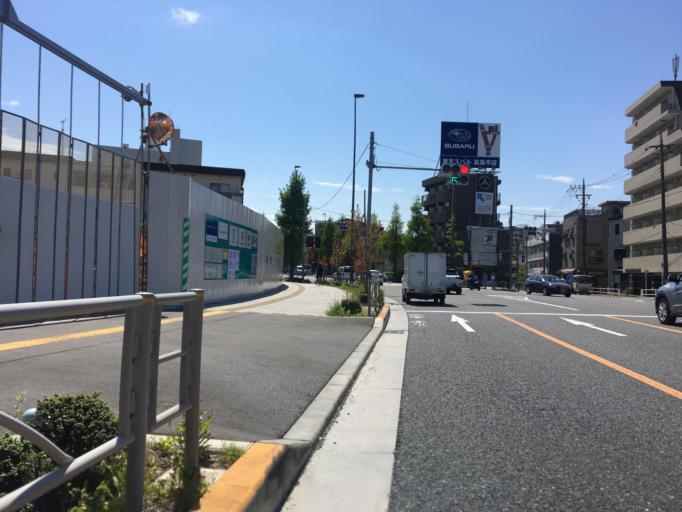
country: JP
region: Saitama
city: Shimotoda
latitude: 35.7886
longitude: 139.6849
